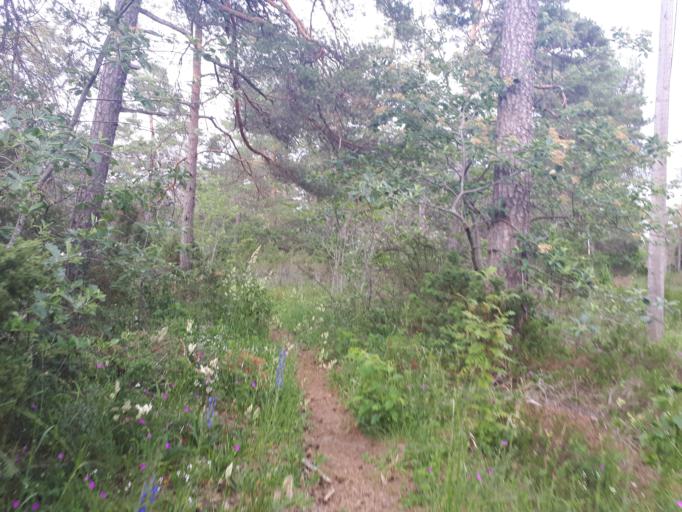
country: SE
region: Gotland
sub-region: Gotland
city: Visby
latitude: 57.6003
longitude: 18.3035
